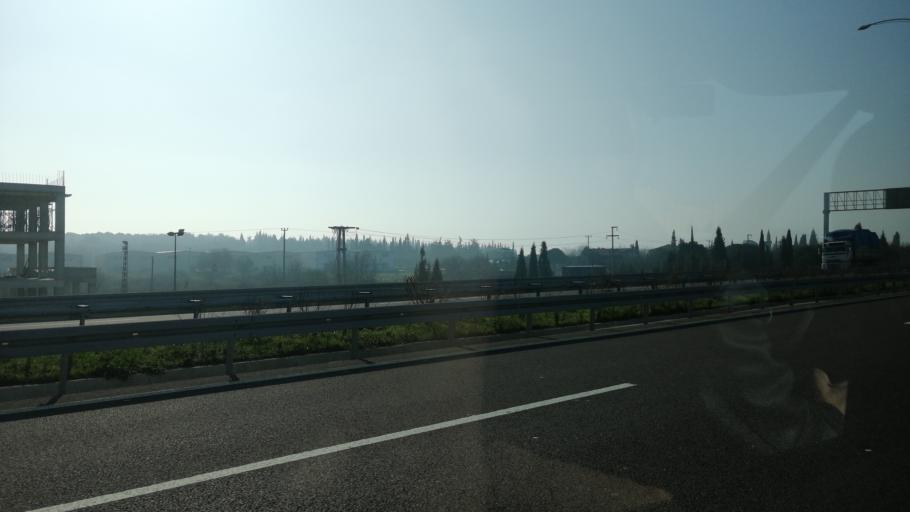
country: TR
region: Yalova
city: Altinova
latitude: 40.7275
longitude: 29.5048
